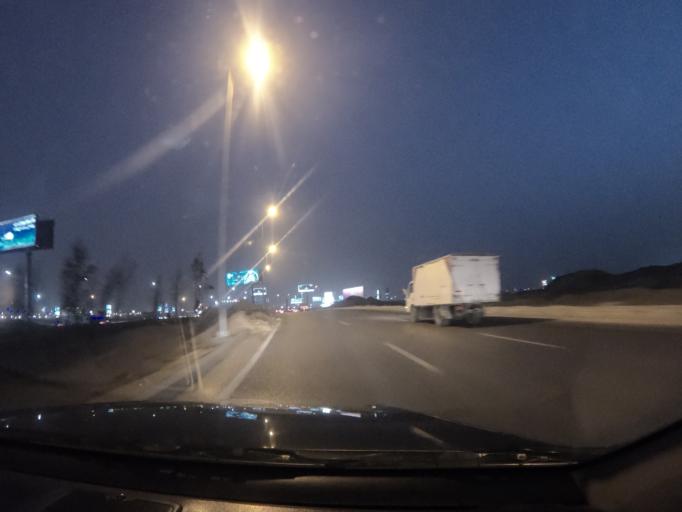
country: EG
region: Muhafazat al Qahirah
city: Cairo
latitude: 30.0222
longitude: 31.4008
